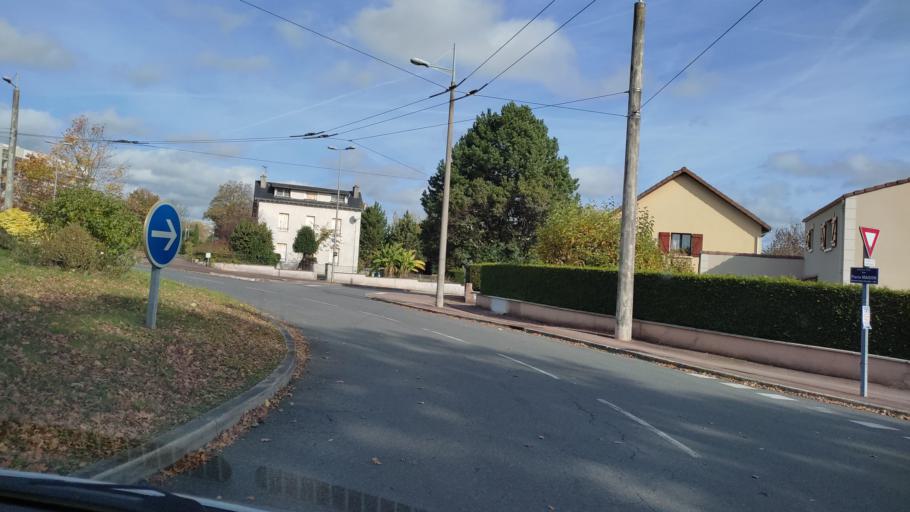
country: FR
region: Limousin
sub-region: Departement de la Haute-Vienne
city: Isle
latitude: 45.8133
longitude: 1.2285
